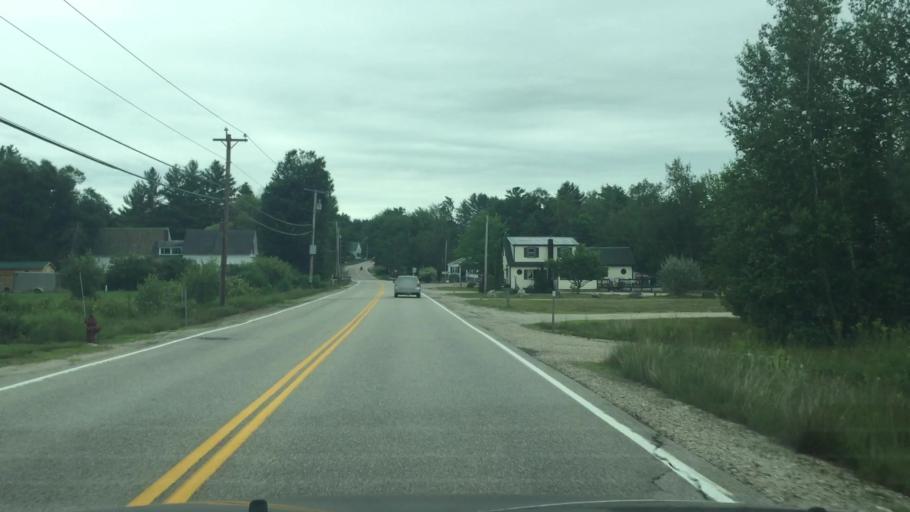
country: US
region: New Hampshire
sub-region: Carroll County
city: Conway
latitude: 43.9712
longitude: -71.1136
